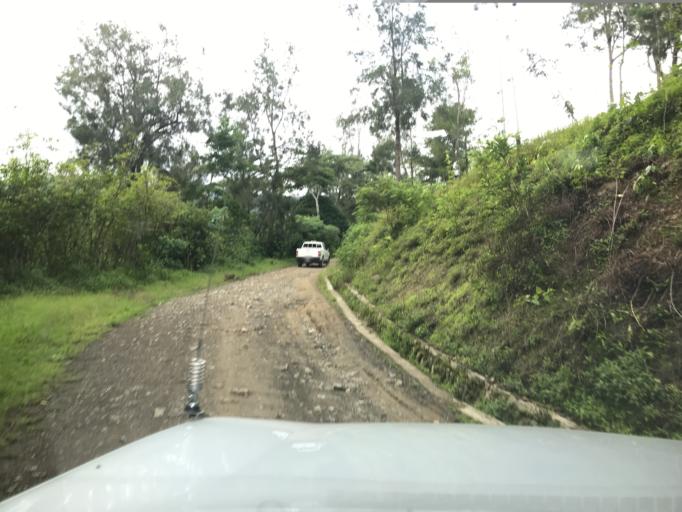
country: TL
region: Aileu
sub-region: Aileu Villa
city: Aileu
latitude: -8.8521
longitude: 125.5828
